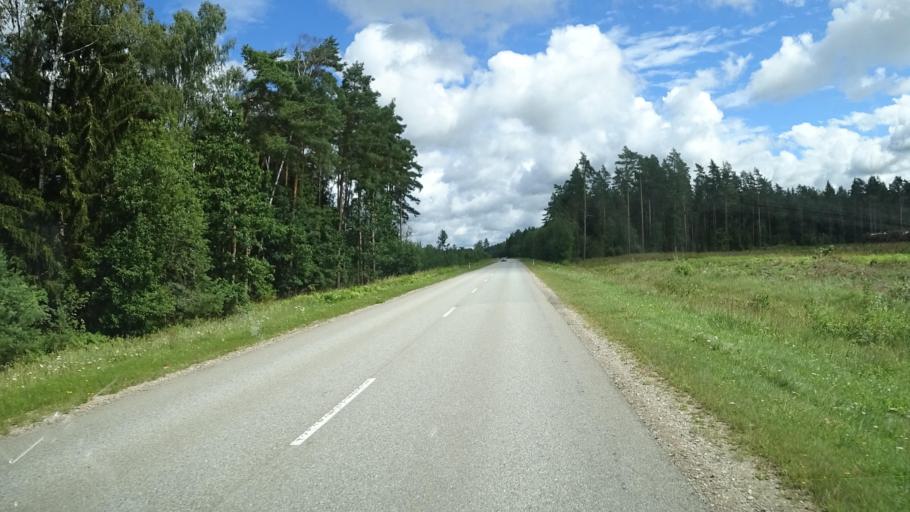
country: LV
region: Pavilostas
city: Pavilosta
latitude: 56.7319
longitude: 21.2109
